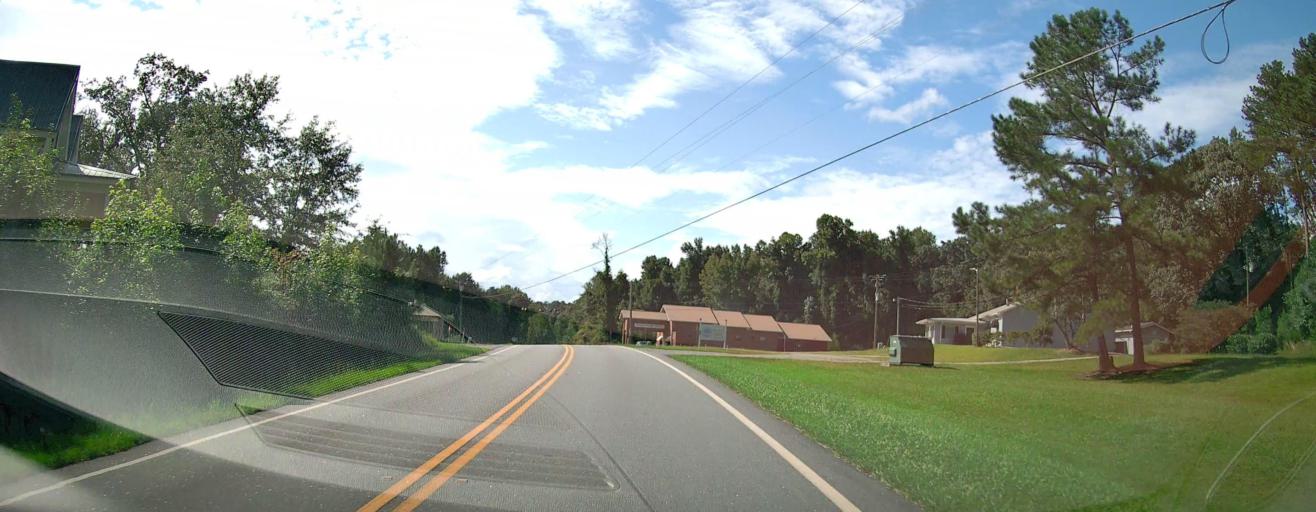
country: US
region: Georgia
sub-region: Upson County
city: Hannahs Mill
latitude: 32.9311
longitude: -84.4448
